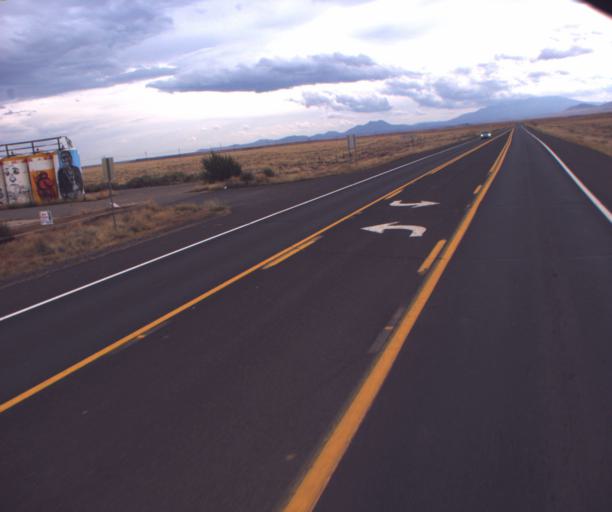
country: US
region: Arizona
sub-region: Coconino County
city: Tuba City
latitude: 35.7421
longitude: -111.4752
